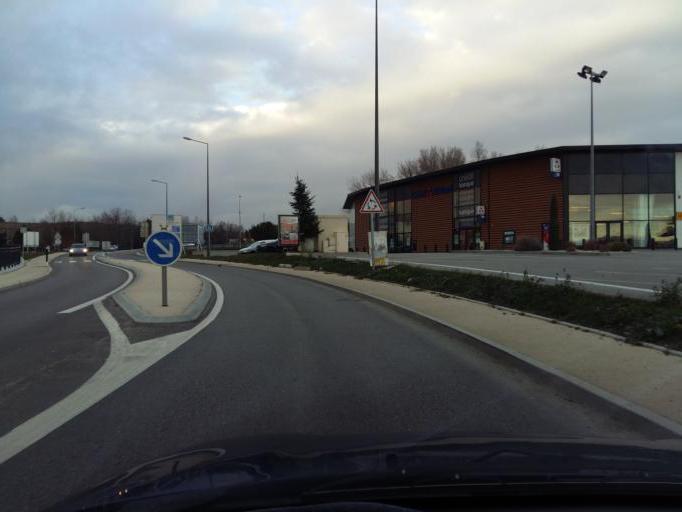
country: FR
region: Rhone-Alpes
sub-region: Departement de la Drome
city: Mercurol
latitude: 45.0689
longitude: 4.8644
